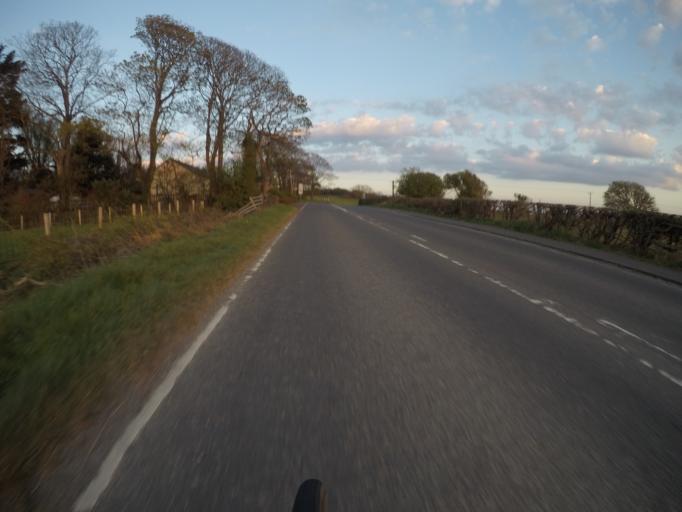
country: GB
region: Scotland
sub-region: South Ayrshire
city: Troon
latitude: 55.5564
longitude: -4.6265
